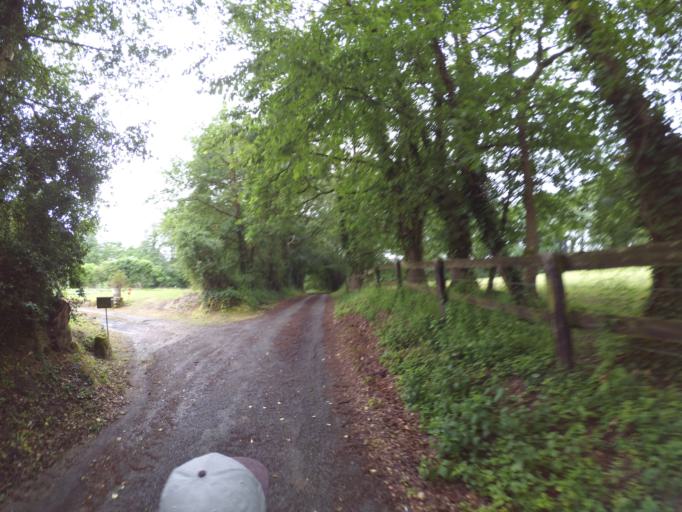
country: FR
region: Pays de la Loire
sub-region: Departement de la Vendee
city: La Roche-sur-Yon
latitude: 46.6289
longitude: -1.4244
